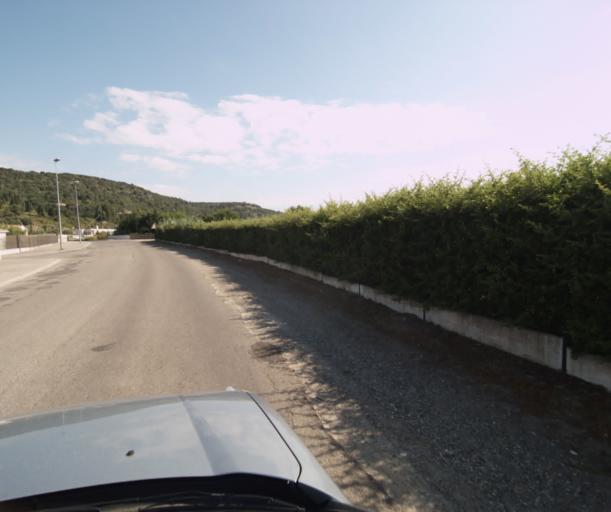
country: FR
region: Languedoc-Roussillon
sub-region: Departement de l'Aude
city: Limoux
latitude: 43.0728
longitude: 2.2176
